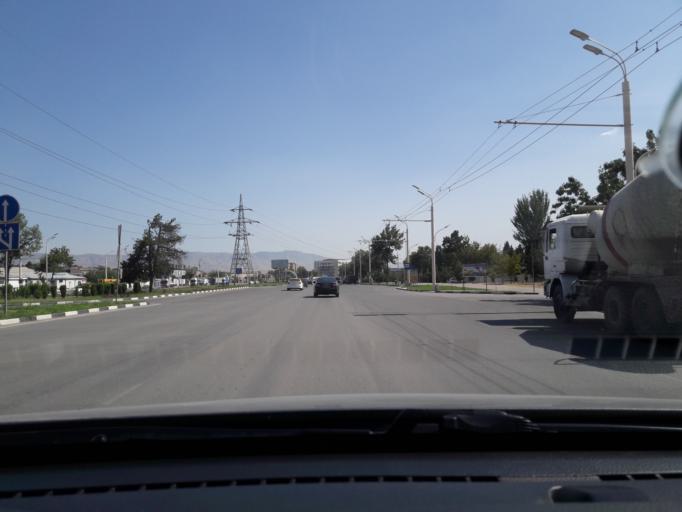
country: TJ
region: Dushanbe
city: Dushanbe
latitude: 38.5410
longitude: 68.7409
